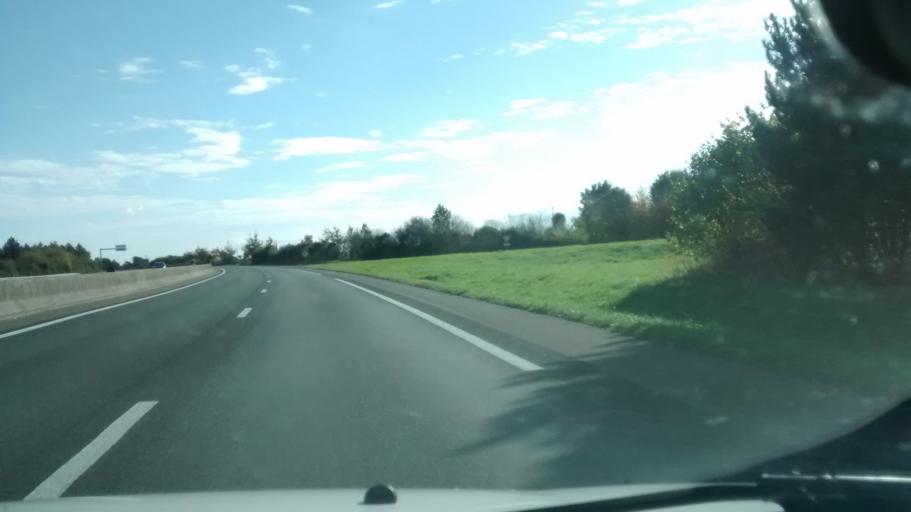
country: FR
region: Pays de la Loire
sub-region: Departement de Maine-et-Loire
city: Pouance
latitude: 47.7371
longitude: -1.1489
